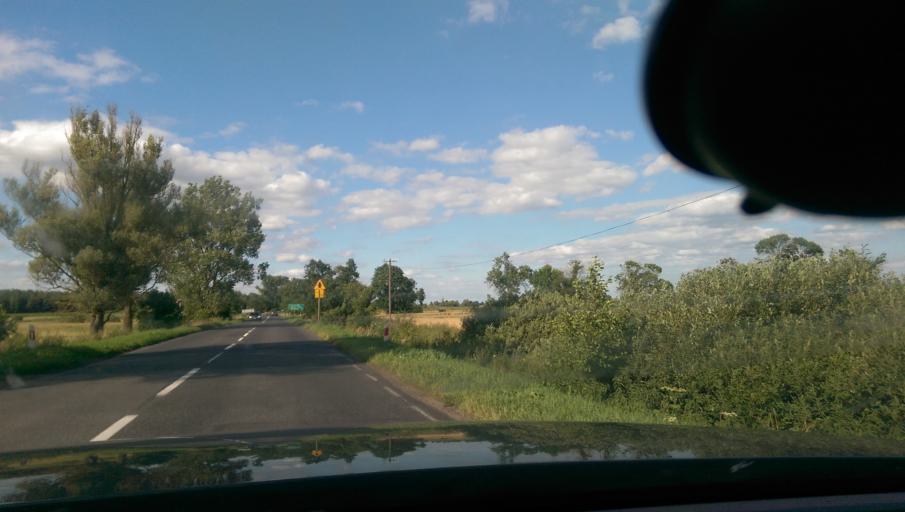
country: PL
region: Lubusz
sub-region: Powiat sulecinski
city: Krzeszyce
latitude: 52.5607
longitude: 14.9600
